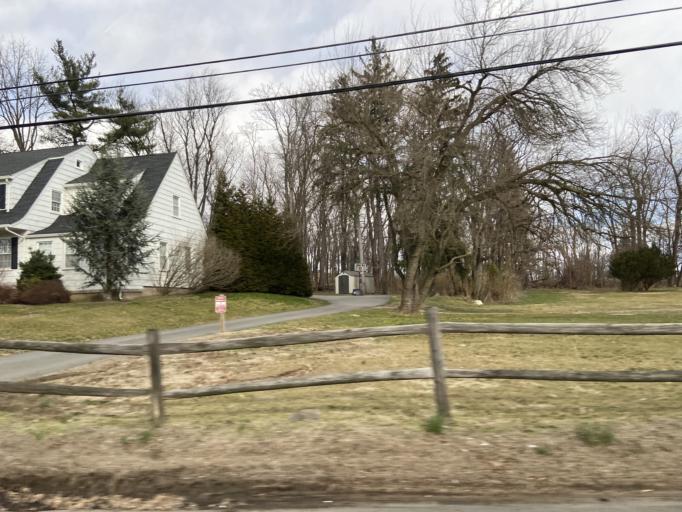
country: US
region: New Jersey
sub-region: Bergen County
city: Paramus
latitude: 40.9279
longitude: -74.0906
